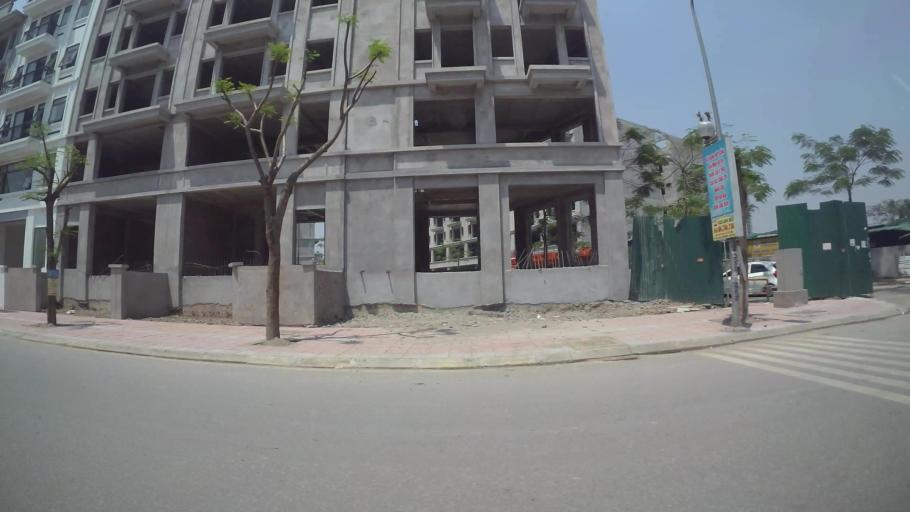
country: VN
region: Ha Noi
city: Hoan Kiem
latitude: 21.0375
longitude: 105.8805
